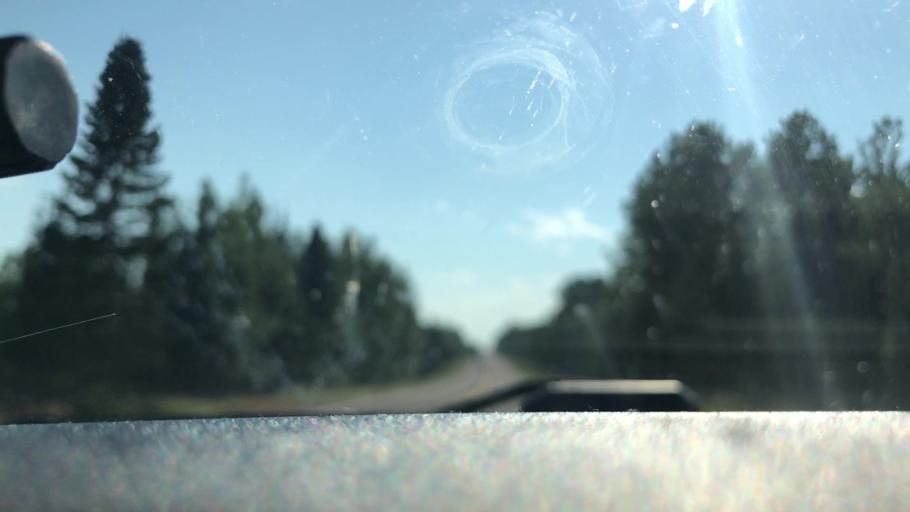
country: US
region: Minnesota
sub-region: Cook County
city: Grand Marais
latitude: 47.8268
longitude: -90.0115
